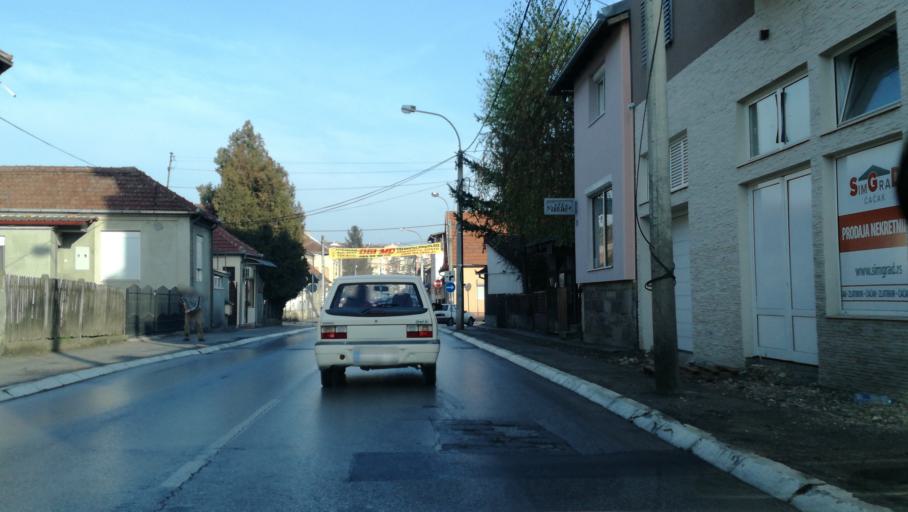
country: RS
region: Central Serbia
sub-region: Moravicki Okrug
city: Cacak
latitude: 43.8931
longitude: 20.3519
